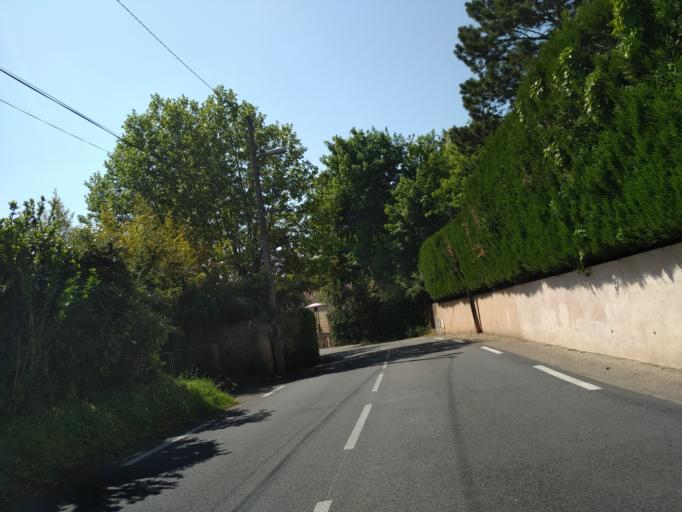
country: FR
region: Rhone-Alpes
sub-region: Departement du Rhone
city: Fontaines-sur-Saone
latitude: 45.8185
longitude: 4.8190
